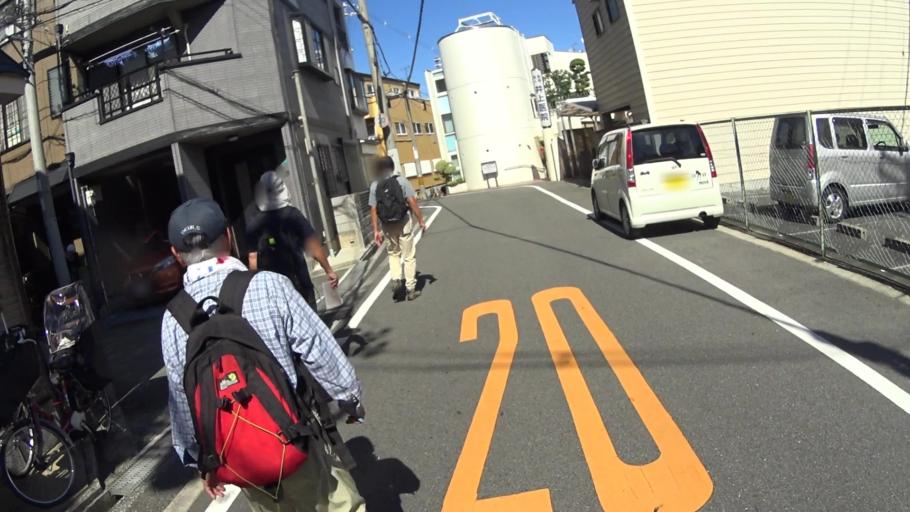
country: JP
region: Osaka
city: Yao
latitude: 34.6275
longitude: 135.5565
